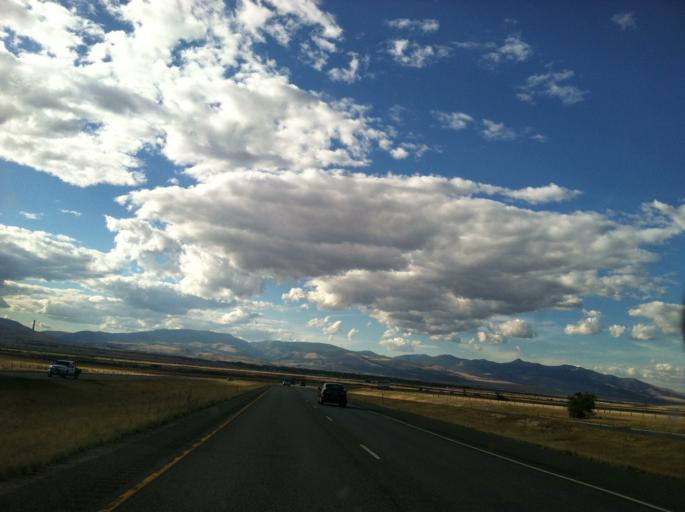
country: US
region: Montana
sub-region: Deer Lodge County
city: Warm Springs
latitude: 46.0694
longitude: -112.7800
